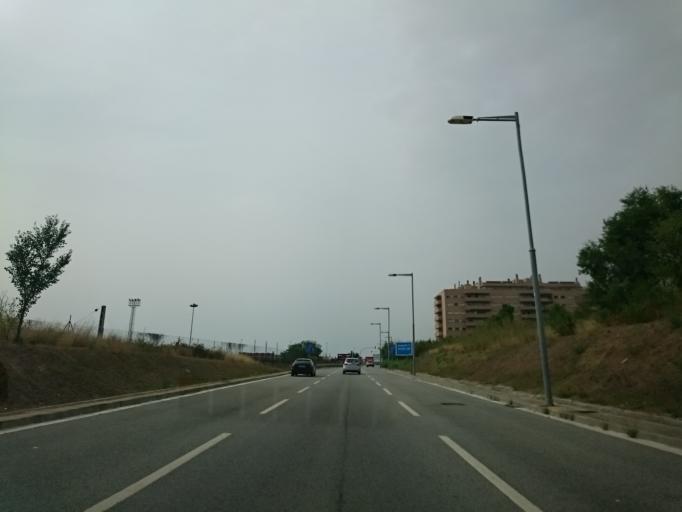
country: ES
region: Catalonia
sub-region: Provincia de Barcelona
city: Sant Andreu de Palomar
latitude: 41.4447
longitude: 2.1943
